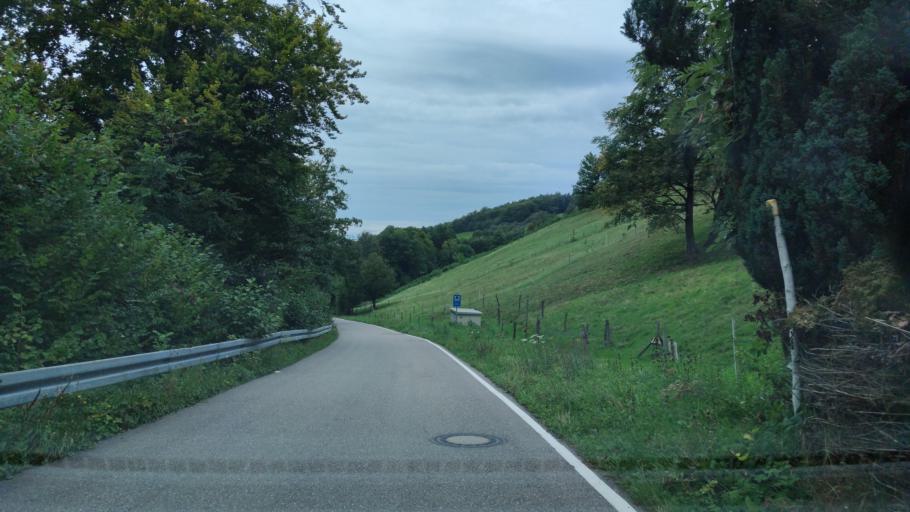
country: DE
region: Baden-Wuerttemberg
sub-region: Freiburg Region
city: Lauf
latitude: 48.6375
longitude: 8.1583
